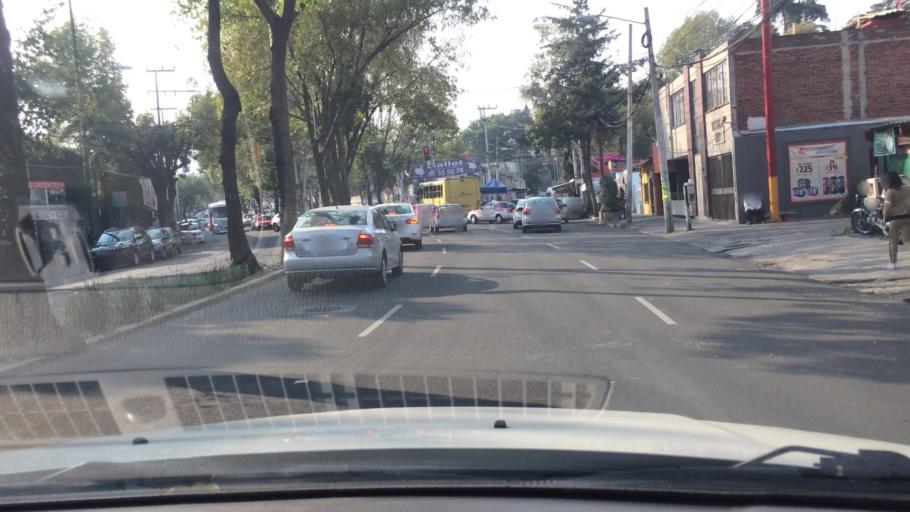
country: MX
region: Mexico City
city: Tlalpan
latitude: 19.2950
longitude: -99.1749
